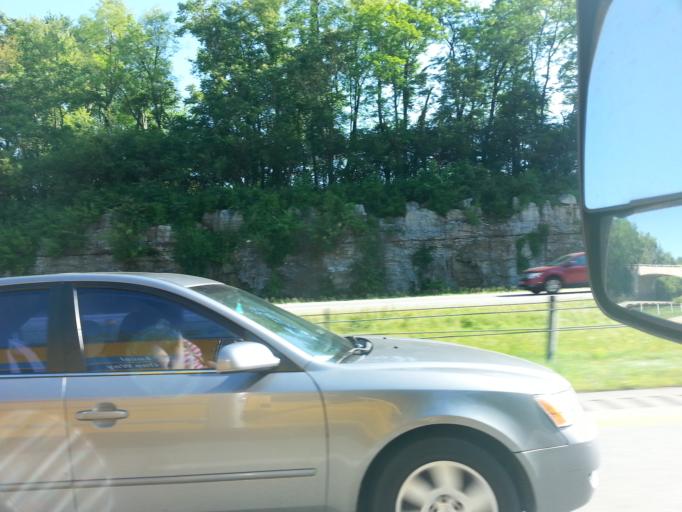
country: US
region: Kentucky
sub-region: Jefferson County
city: Saint Matthews
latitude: 38.2393
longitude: -85.6753
